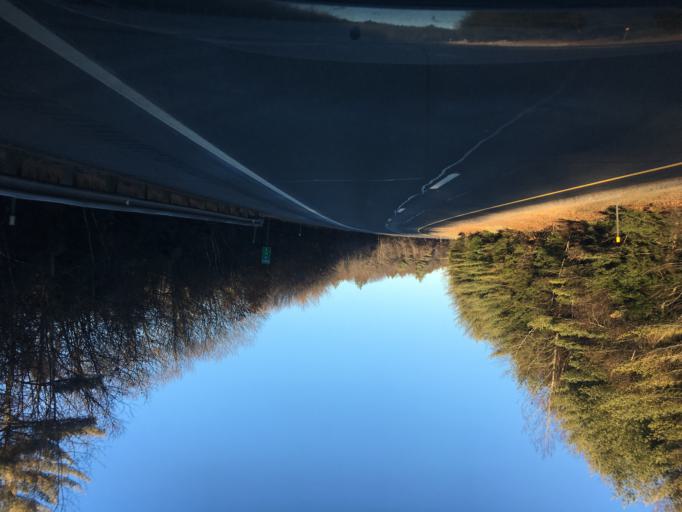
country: US
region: New Hampshire
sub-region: Belknap County
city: Sanbornton
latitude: 43.4908
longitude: -71.5959
